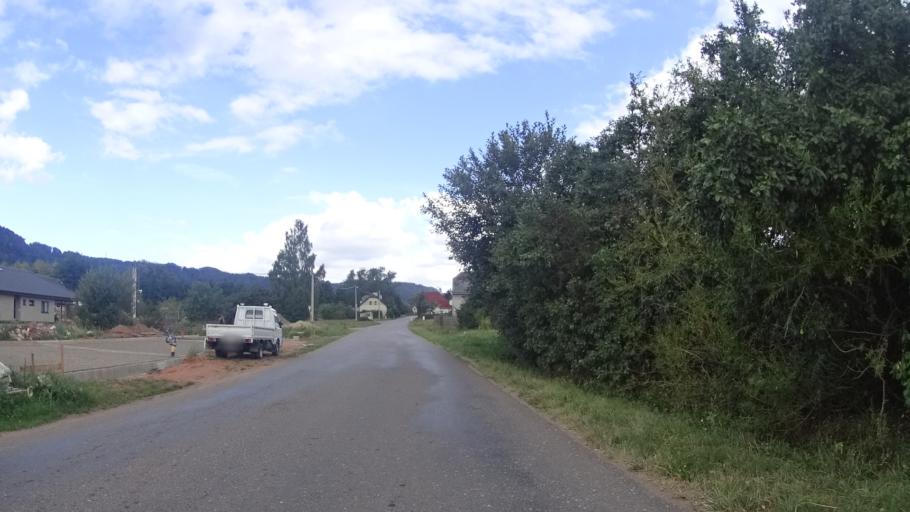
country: CZ
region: Pardubicky
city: Dolni Cermna
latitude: 49.9417
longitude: 16.5233
